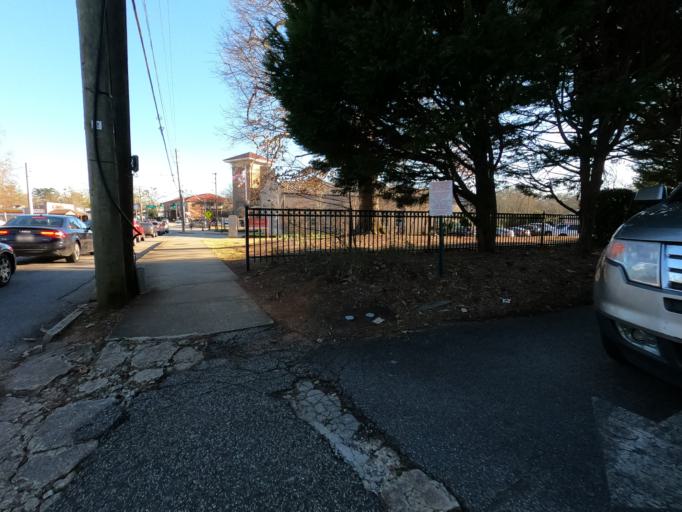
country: US
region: Georgia
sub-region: Clarke County
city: Athens
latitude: 33.9398
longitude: -83.3871
